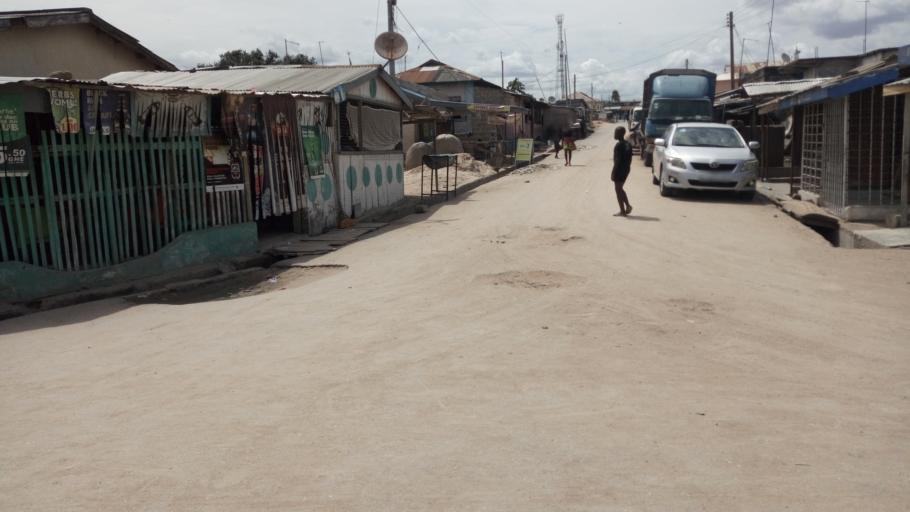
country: GH
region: Central
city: Winneba
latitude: 5.3465
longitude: -0.6200
